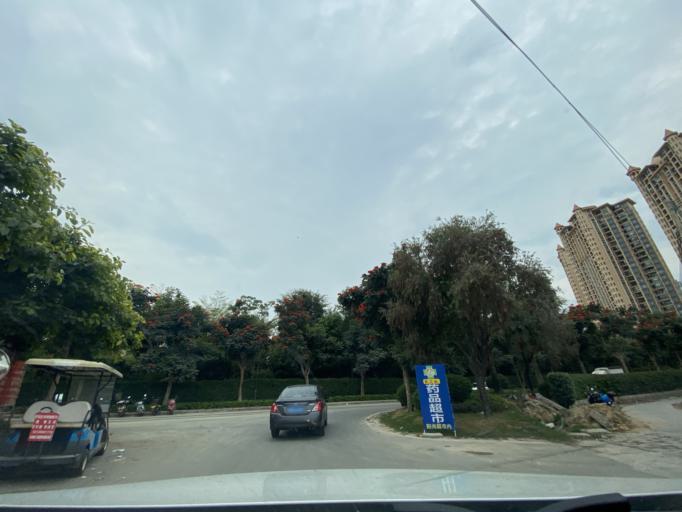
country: CN
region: Hainan
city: Yingzhou
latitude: 18.3892
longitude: 109.8427
